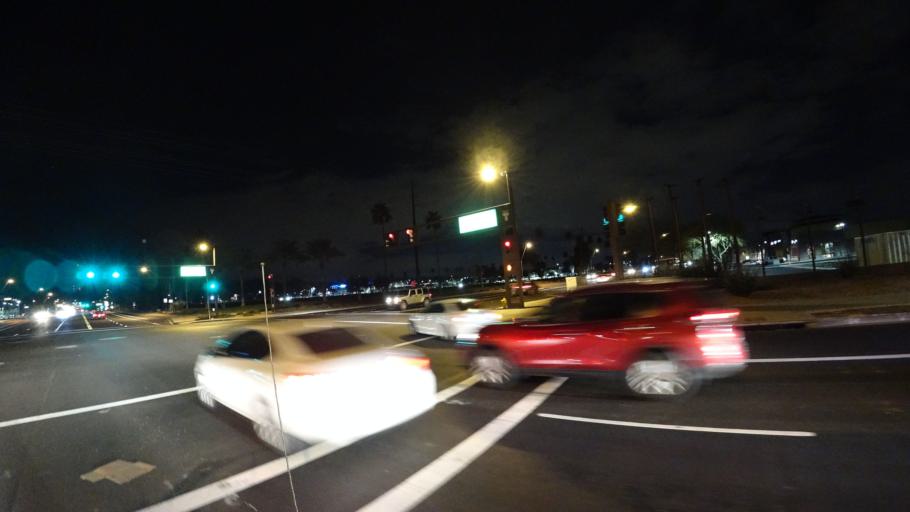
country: US
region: Arizona
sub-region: Maricopa County
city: Guadalupe
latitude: 33.3346
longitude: -111.9629
